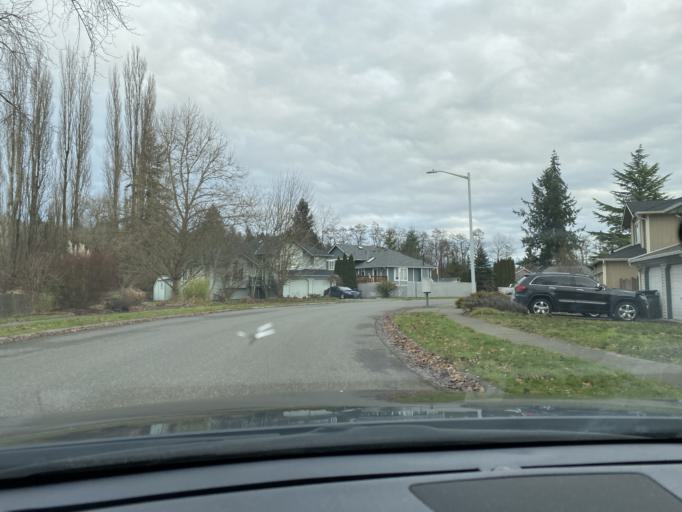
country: US
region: Washington
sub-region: Snohomish County
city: Marysville
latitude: 48.0830
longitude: -122.1586
